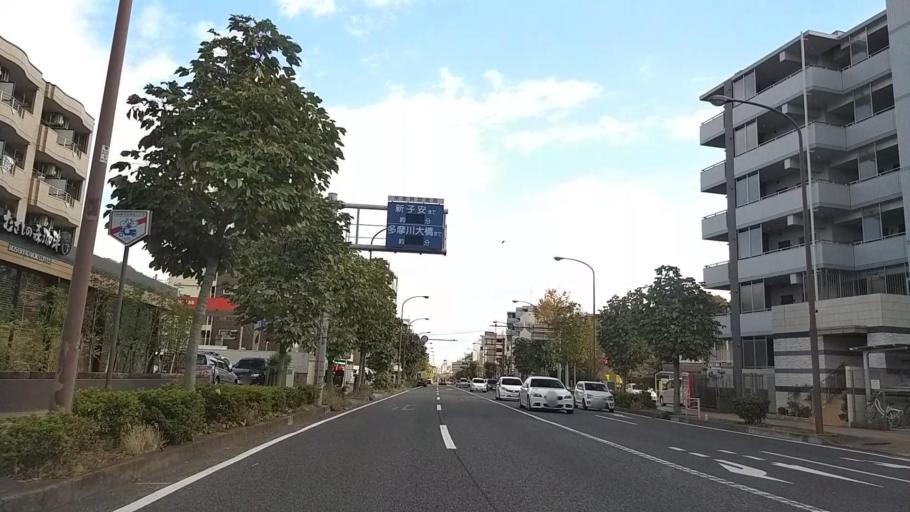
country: JP
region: Kanagawa
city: Yokohama
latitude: 35.4765
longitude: 139.6029
